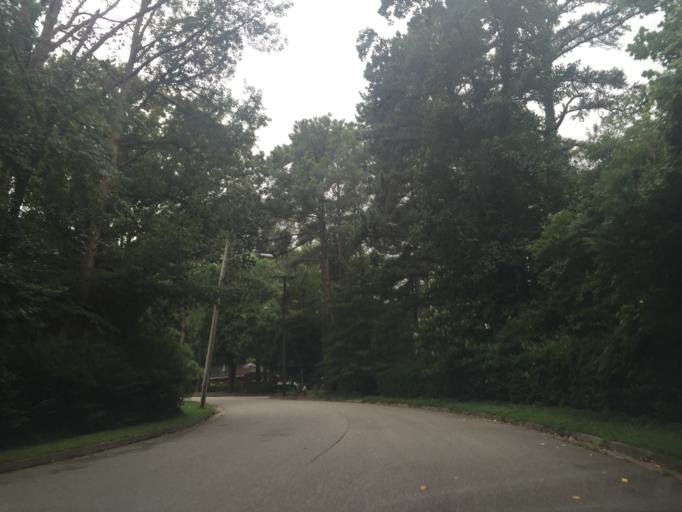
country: US
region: Virginia
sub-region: City of Newport News
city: Newport News
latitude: 37.0692
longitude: -76.5038
